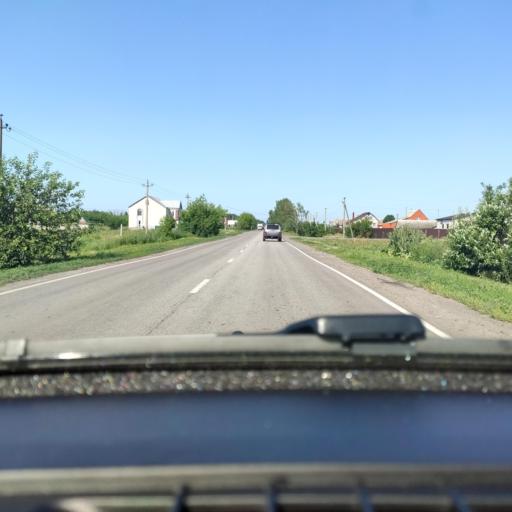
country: RU
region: Voronezj
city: Panino
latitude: 51.6509
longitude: 40.1144
